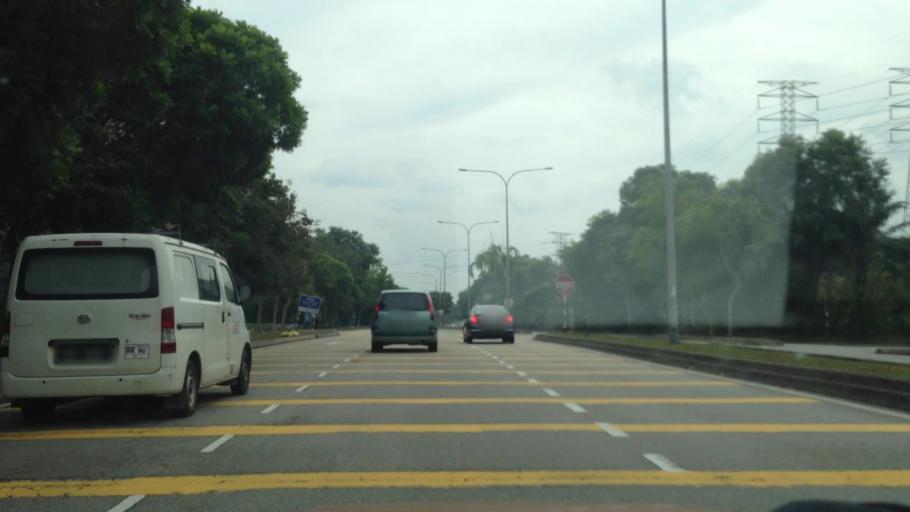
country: MY
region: Selangor
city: Subang Jaya
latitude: 3.0496
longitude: 101.5701
